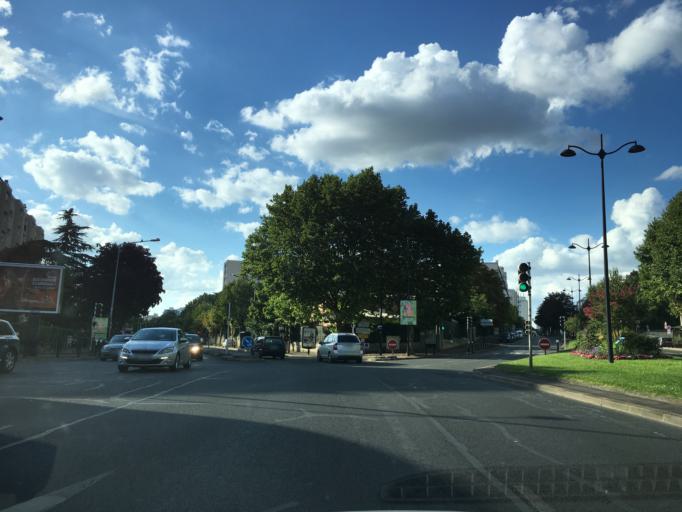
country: FR
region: Ile-de-France
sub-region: Departement du Val-de-Marne
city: Joinville-le-Pont
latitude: 48.8116
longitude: 2.4690
